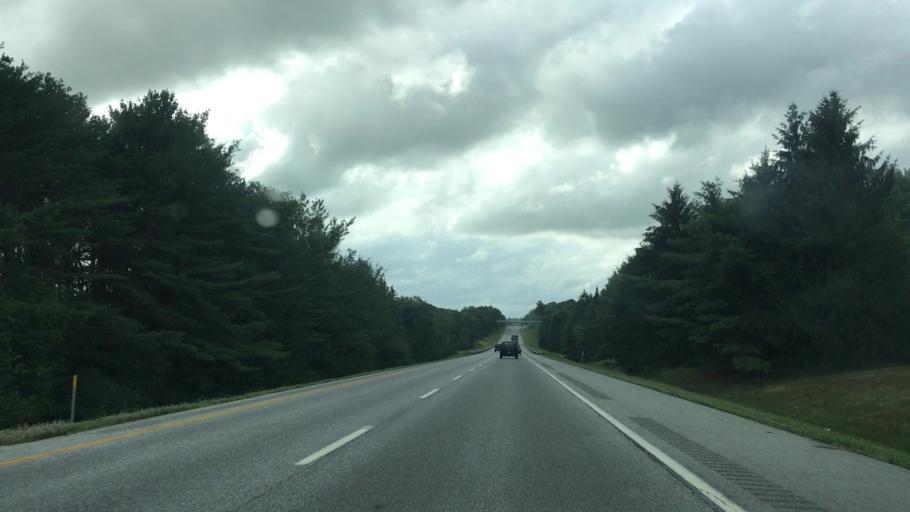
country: US
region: Maine
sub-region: Penobscot County
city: Plymouth
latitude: 44.7985
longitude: -69.2142
